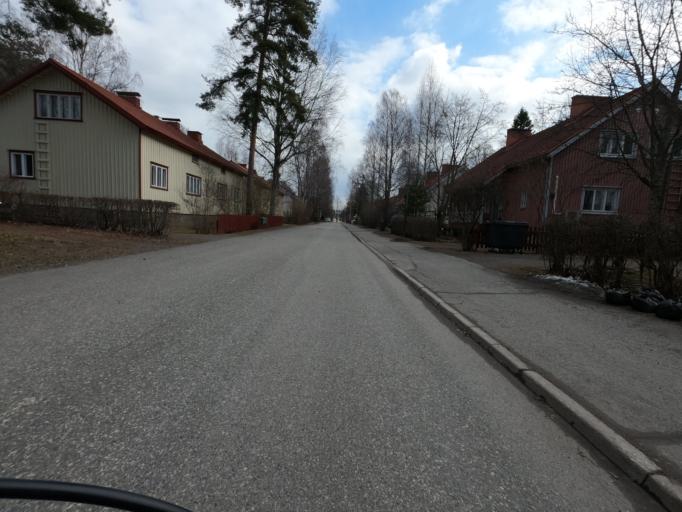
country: FI
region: North Karelia
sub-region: Joensuu
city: Joensuu
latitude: 62.6091
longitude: 29.7603
